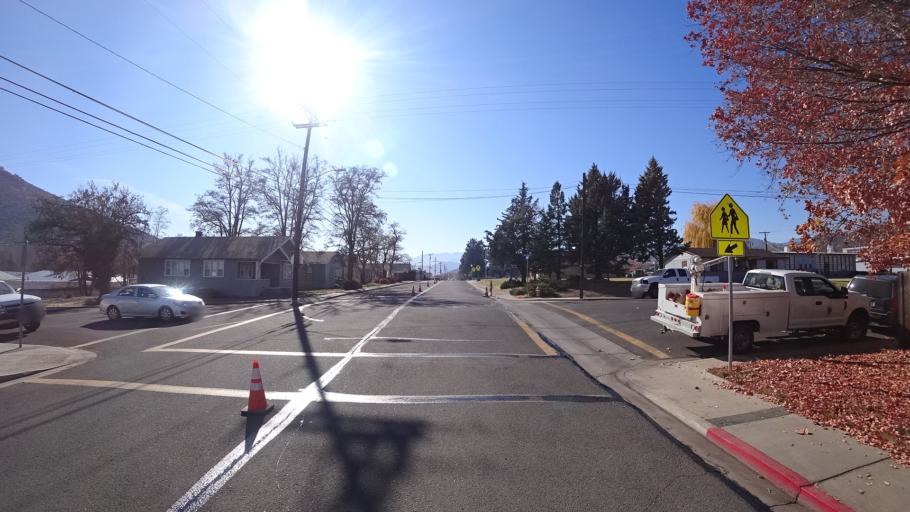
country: US
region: California
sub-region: Siskiyou County
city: Yreka
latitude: 41.7281
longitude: -122.6388
